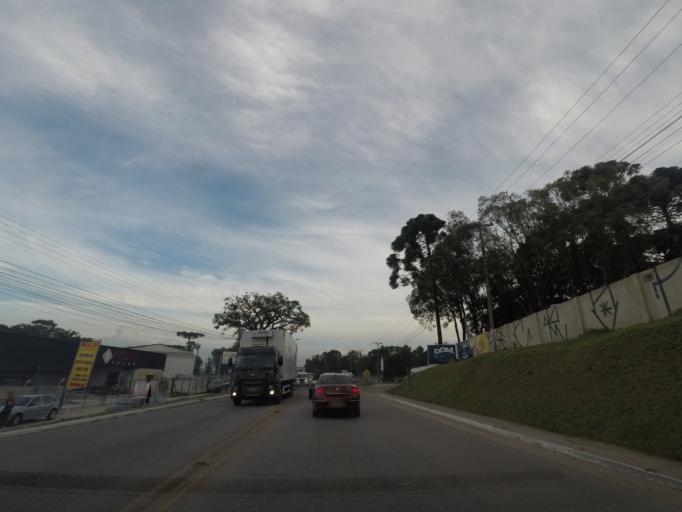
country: BR
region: Parana
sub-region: Colombo
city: Colombo
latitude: -25.3491
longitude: -49.2214
